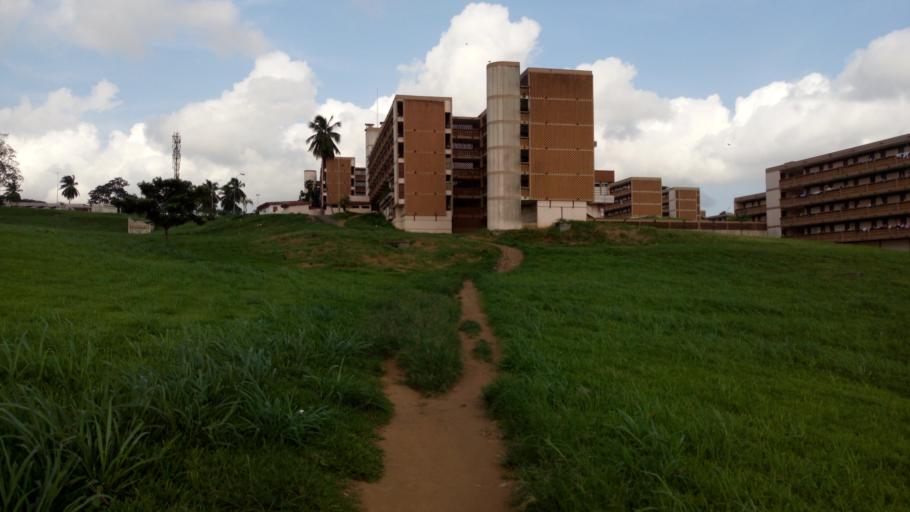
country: CI
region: Lagunes
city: Abidjan
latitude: 5.3427
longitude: -3.9908
